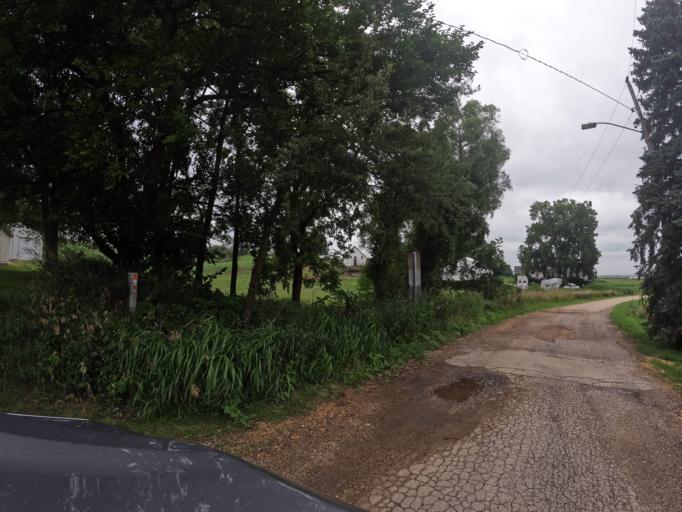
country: US
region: Iowa
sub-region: Clinton County
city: De Witt
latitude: 41.9144
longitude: -90.6015
